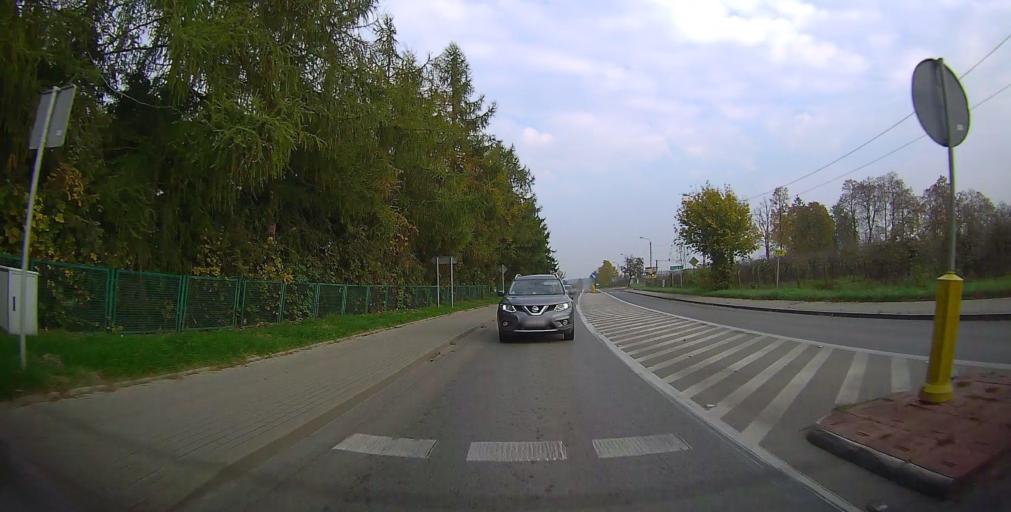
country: PL
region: Masovian Voivodeship
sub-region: Powiat grojecki
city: Belsk Duzy
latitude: 51.7765
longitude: 20.7703
